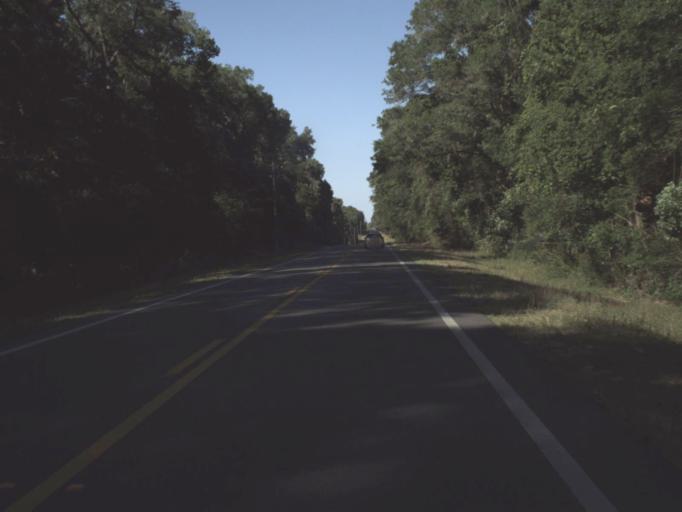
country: US
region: Florida
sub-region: Marion County
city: Dunnellon
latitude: 29.1474
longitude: -82.3713
